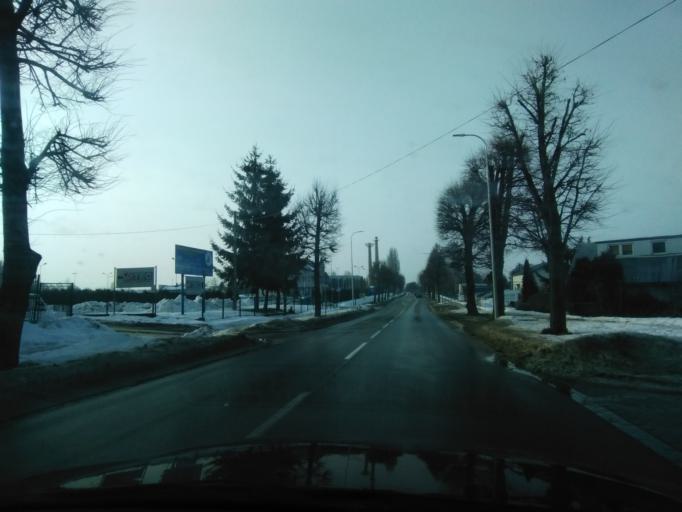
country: PL
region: Subcarpathian Voivodeship
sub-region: Krosno
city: Krosno
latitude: 49.6988
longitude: 21.7447
